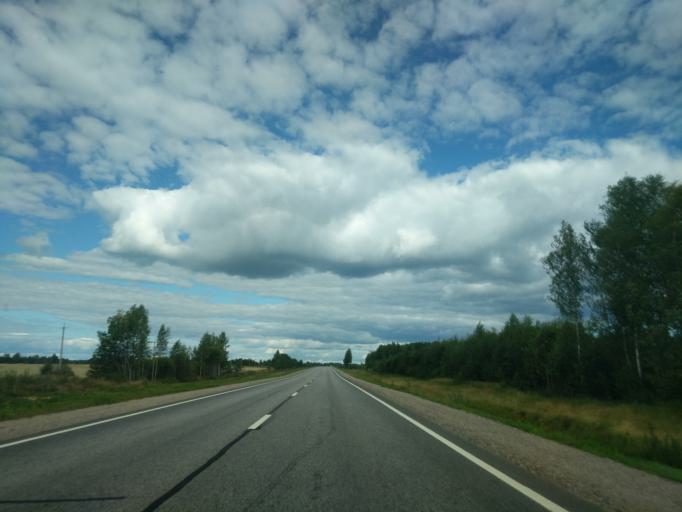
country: RU
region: Kostroma
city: Ostrovskoye
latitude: 57.8145
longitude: 42.4352
